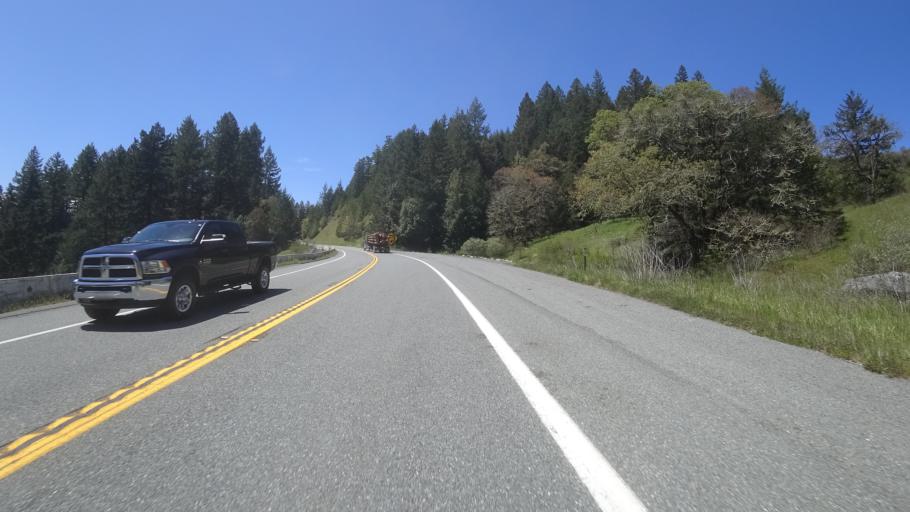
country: US
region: California
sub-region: Humboldt County
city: Willow Creek
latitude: 40.9238
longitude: -123.8046
